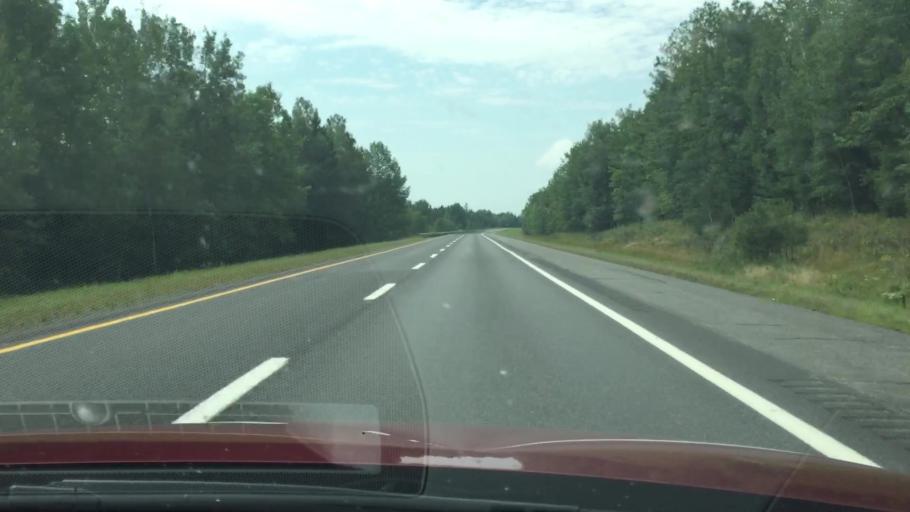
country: US
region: Maine
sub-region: Aroostook County
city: Hodgdon
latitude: 46.1251
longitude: -68.1063
